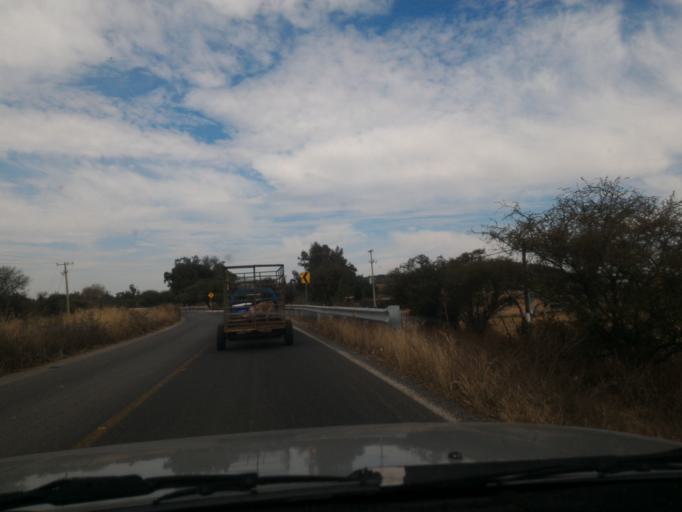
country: MX
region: Guanajuato
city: Ciudad Manuel Doblado
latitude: 20.7960
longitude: -101.9847
